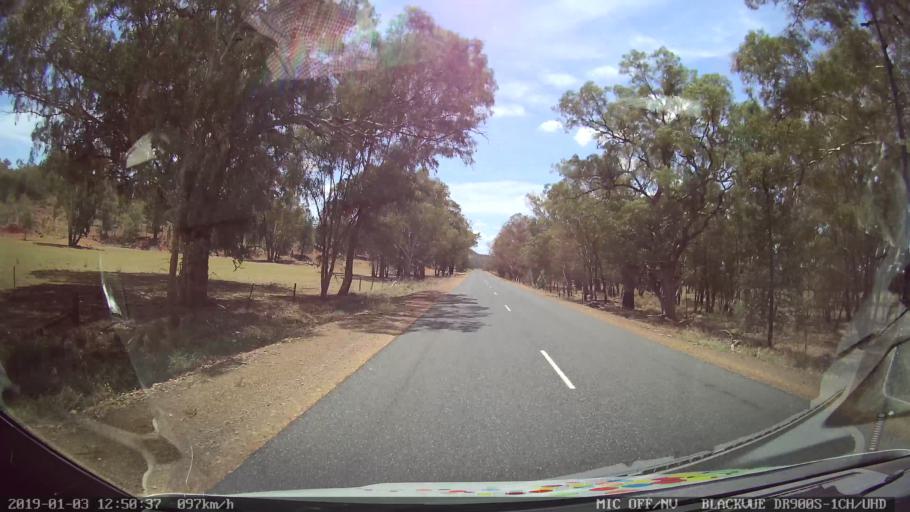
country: AU
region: New South Wales
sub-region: Weddin
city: Grenfell
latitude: -33.6895
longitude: 148.2723
